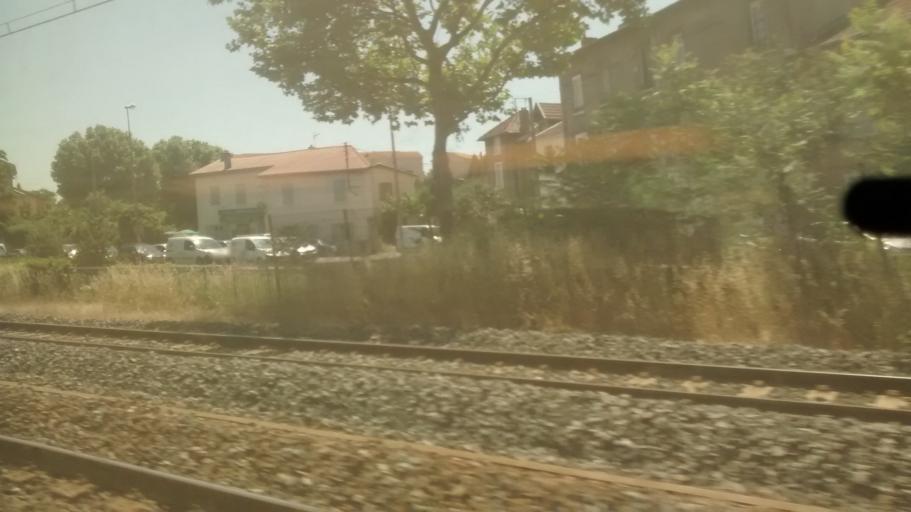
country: FR
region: Rhone-Alpes
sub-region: Departement du Rhone
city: Venissieux
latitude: 45.7073
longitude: 4.8826
